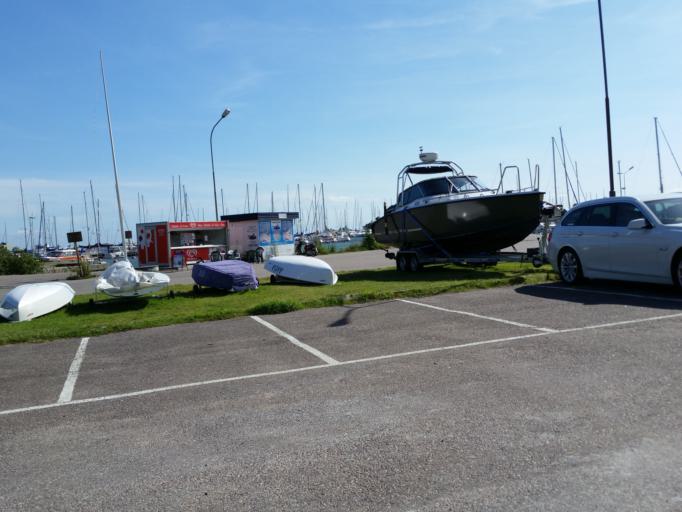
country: FI
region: Uusimaa
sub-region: Raaseporin
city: Hanko
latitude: 59.8210
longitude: 22.9659
